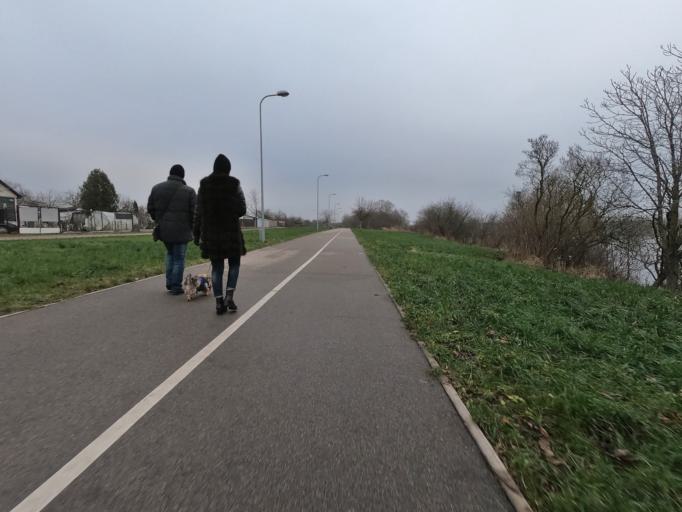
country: LV
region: Kekava
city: Kekava
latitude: 56.8818
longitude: 24.2142
